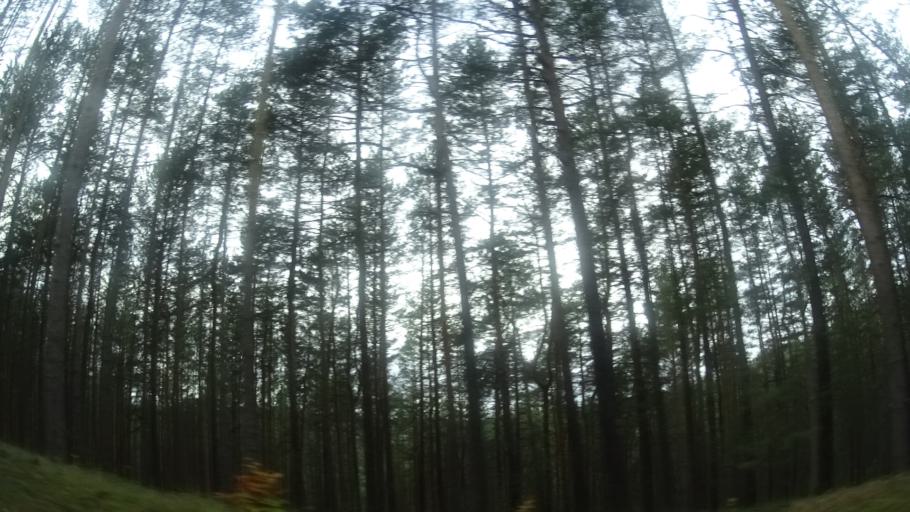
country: DE
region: Thuringia
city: Saalfeld
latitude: 50.6771
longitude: 11.3881
